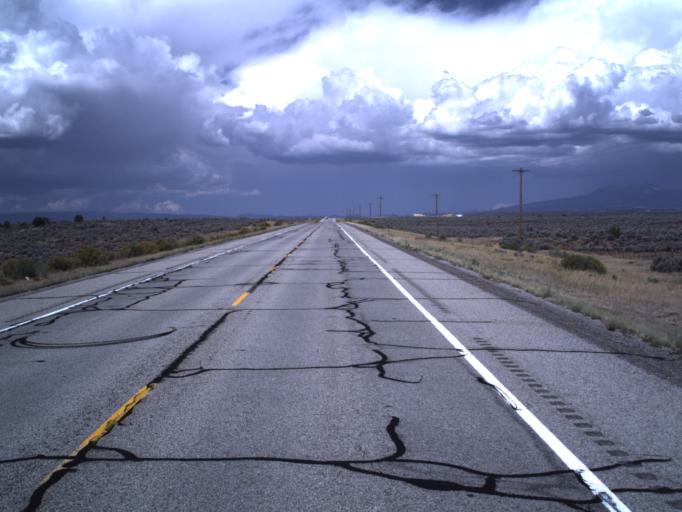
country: US
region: Utah
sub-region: San Juan County
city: Blanding
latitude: 37.5021
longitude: -109.4865
